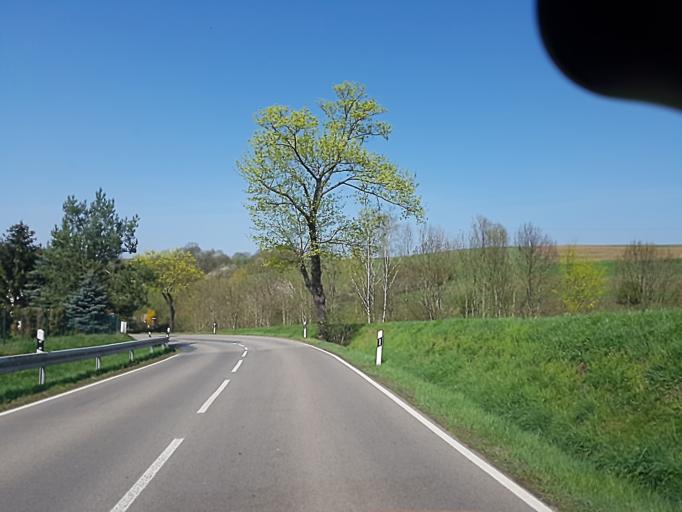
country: DE
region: Saxony
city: Leisnig
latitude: 51.1671
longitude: 12.9314
